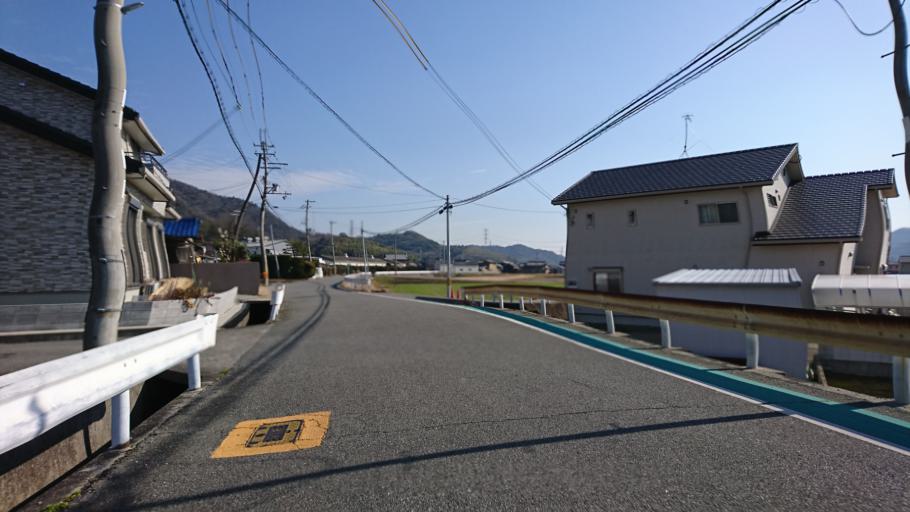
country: JP
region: Hyogo
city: Kakogawacho-honmachi
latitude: 34.8316
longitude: 134.8422
